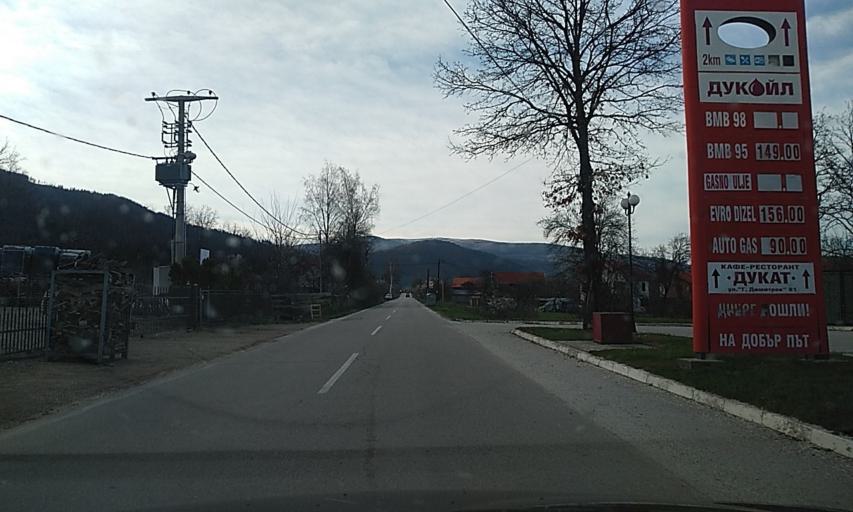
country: RS
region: Central Serbia
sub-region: Pcinjski Okrug
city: Bosilegrad
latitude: 42.4765
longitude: 22.4791
